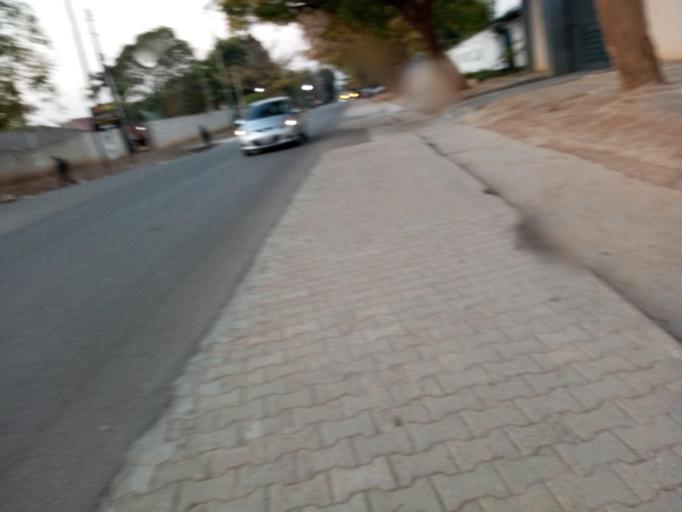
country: ZM
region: Lusaka
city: Lusaka
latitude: -15.4026
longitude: 28.2962
